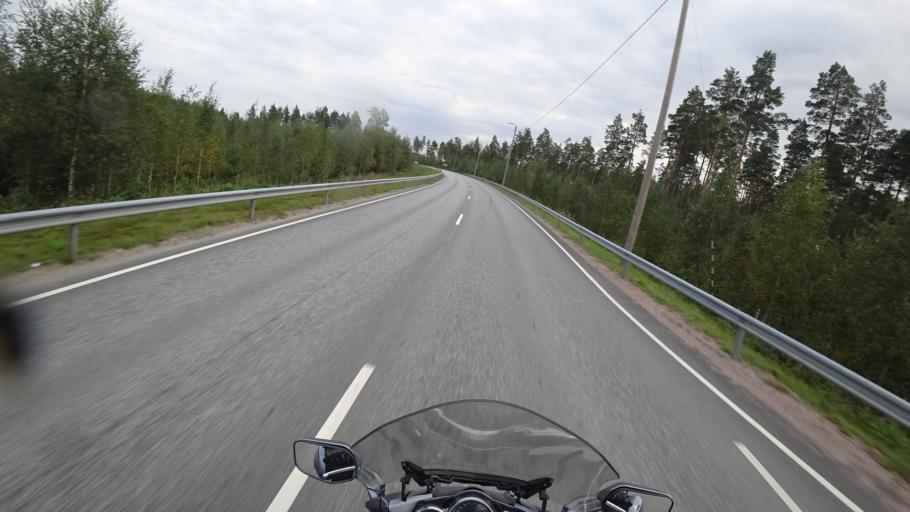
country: FI
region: Uusimaa
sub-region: Raaseporin
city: Karis
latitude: 60.0648
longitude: 23.6301
